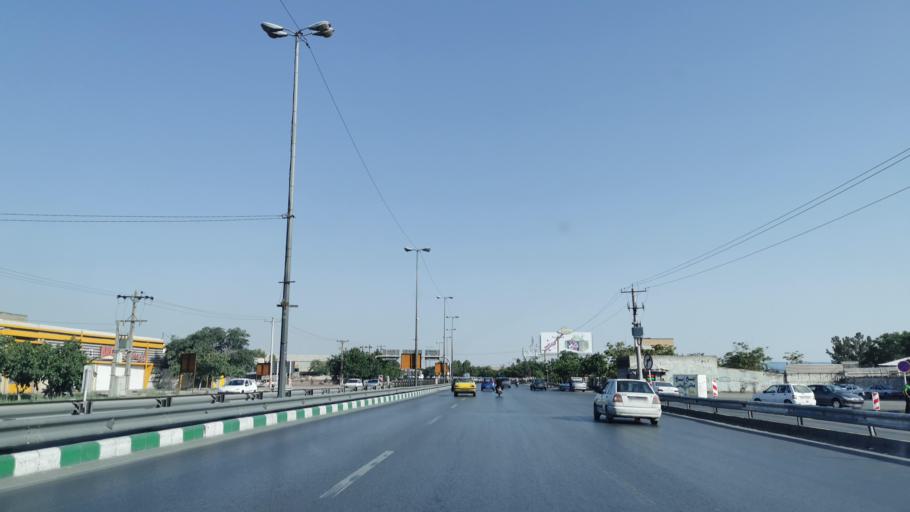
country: IR
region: Razavi Khorasan
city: Mashhad
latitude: 36.3852
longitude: 59.5189
